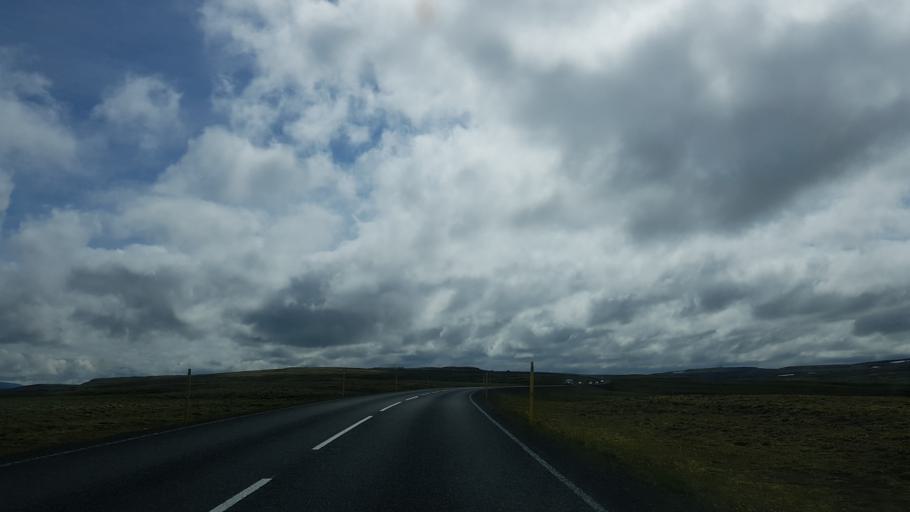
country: IS
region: West
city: Borgarnes
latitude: 65.0056
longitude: -21.0660
